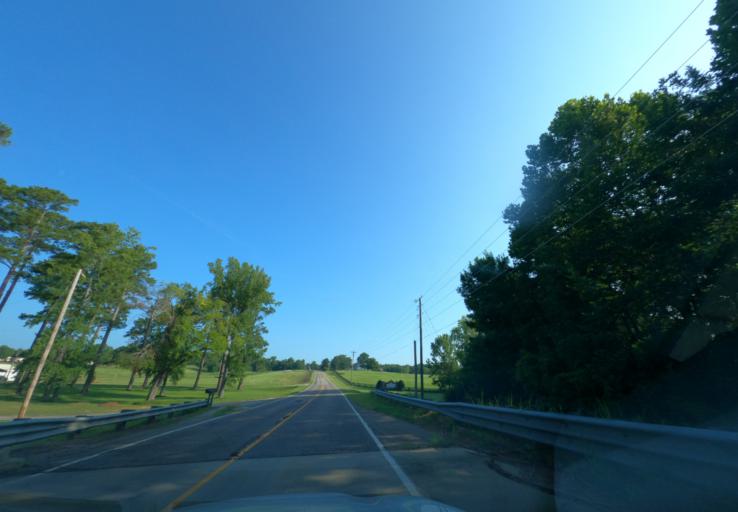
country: US
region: South Carolina
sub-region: Edgefield County
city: Murphys Estates
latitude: 33.6617
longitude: -81.9744
